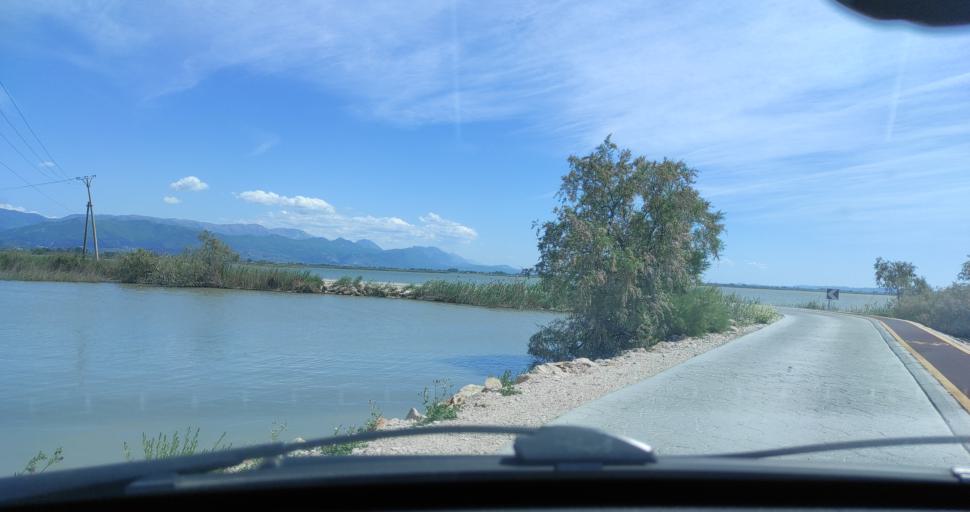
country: AL
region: Lezhe
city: Shengjin
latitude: 41.7465
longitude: 19.5870
